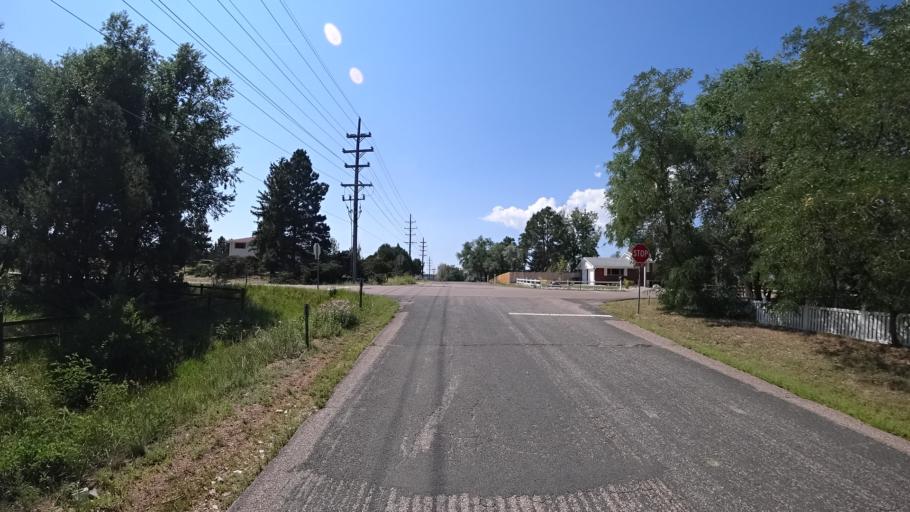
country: US
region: Colorado
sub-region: El Paso County
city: Air Force Academy
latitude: 38.9369
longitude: -104.7937
